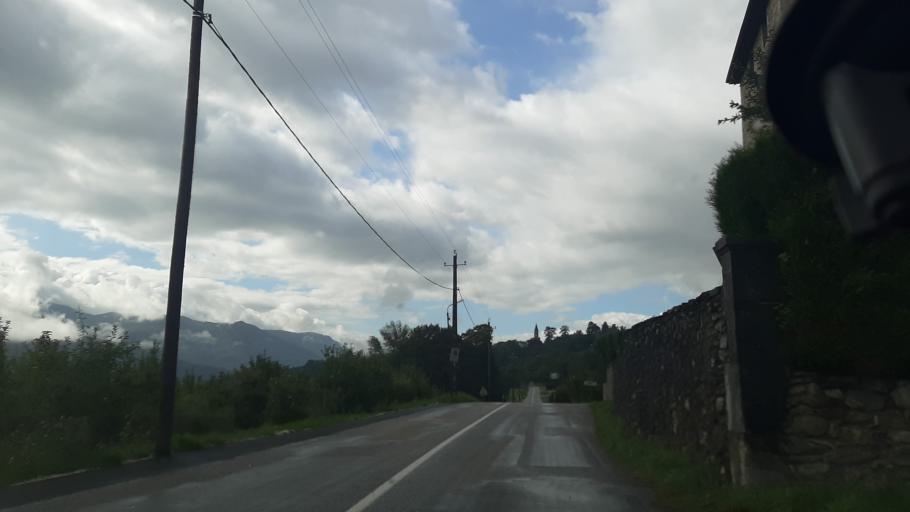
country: FR
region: Rhone-Alpes
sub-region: Departement de la Savoie
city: Frontenex
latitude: 45.6231
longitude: 6.2877
